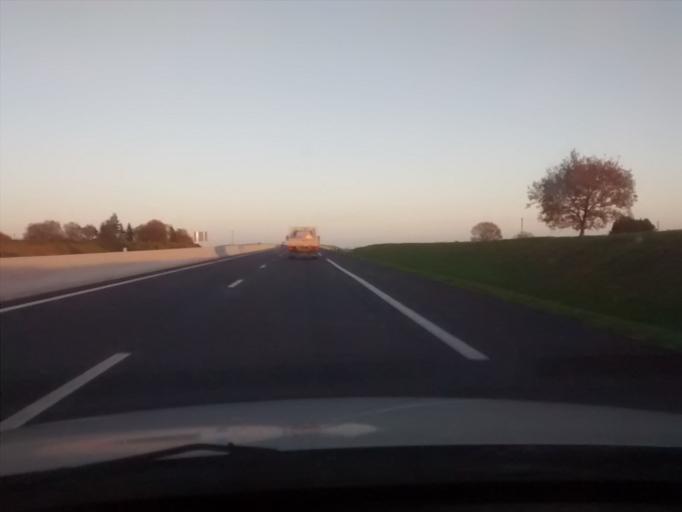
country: FR
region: Pays de la Loire
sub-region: Departement de la Mayenne
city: Loiron
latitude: 48.0736
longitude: -0.9107
